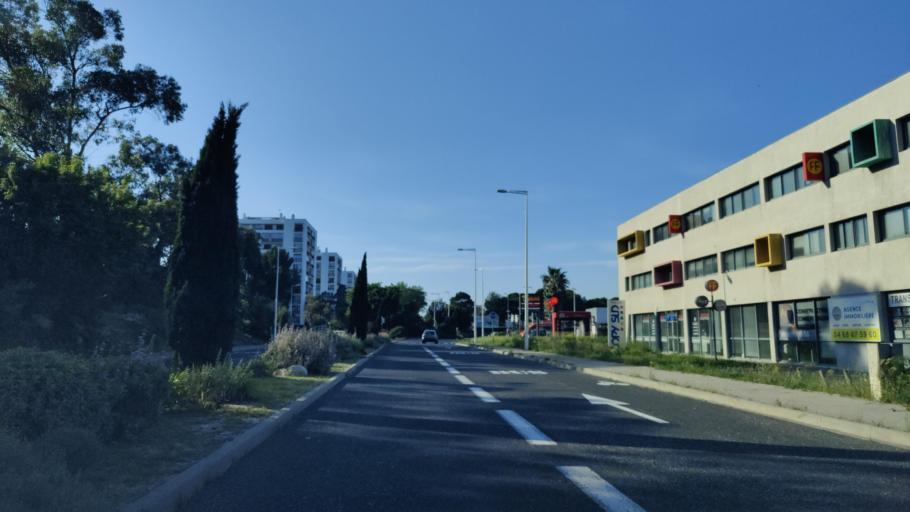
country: FR
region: Languedoc-Roussillon
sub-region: Departement des Pyrenees-Orientales
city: Perpignan
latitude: 42.6800
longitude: 2.9114
